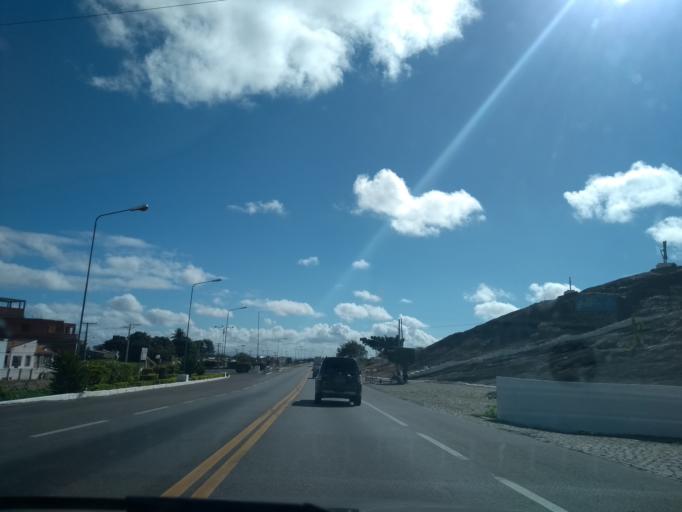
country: BR
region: Bahia
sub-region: Amargosa
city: Amargosa
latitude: -12.8703
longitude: -39.8561
